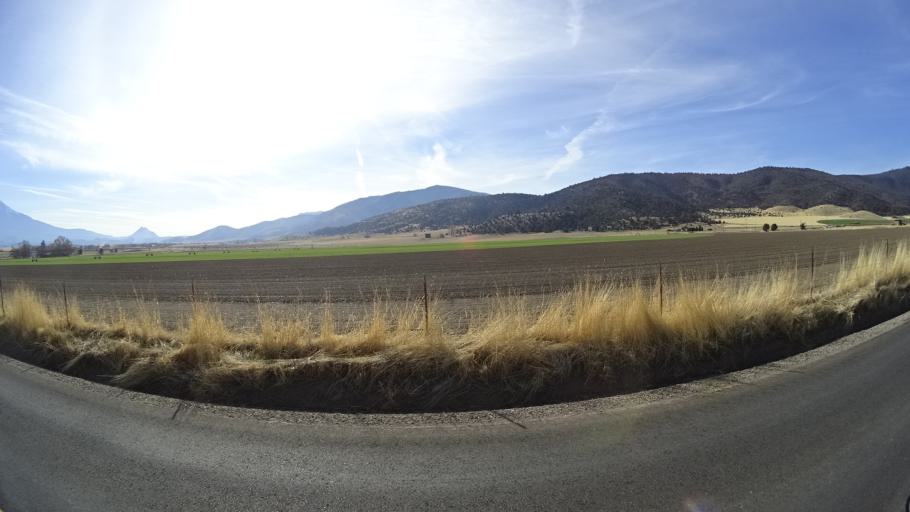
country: US
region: California
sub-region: Siskiyou County
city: Montague
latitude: 41.5381
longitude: -122.5421
